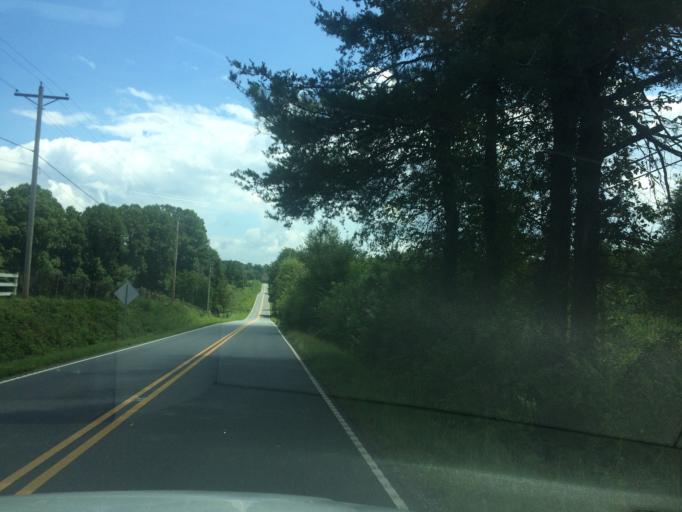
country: US
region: North Carolina
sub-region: Polk County
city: Columbus
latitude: 35.2876
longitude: -82.1377
